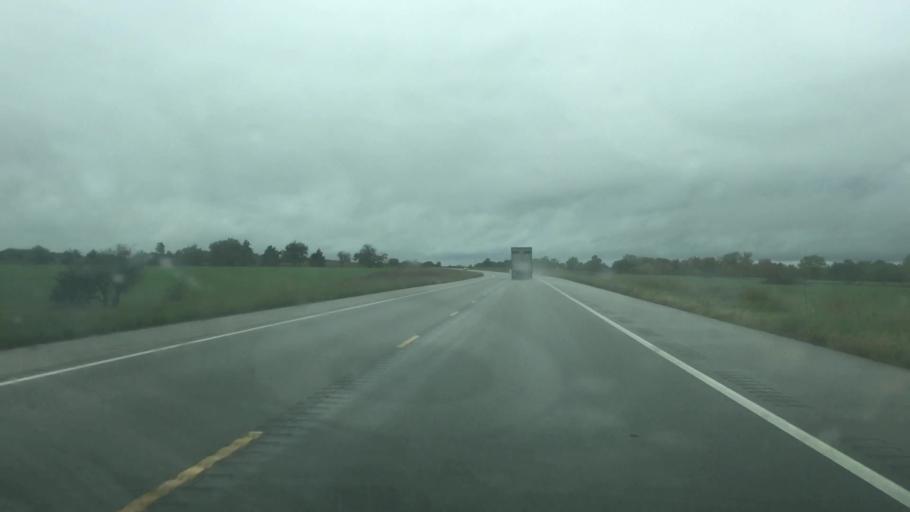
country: US
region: Kansas
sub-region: Allen County
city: Iola
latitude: 38.0776
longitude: -95.3735
